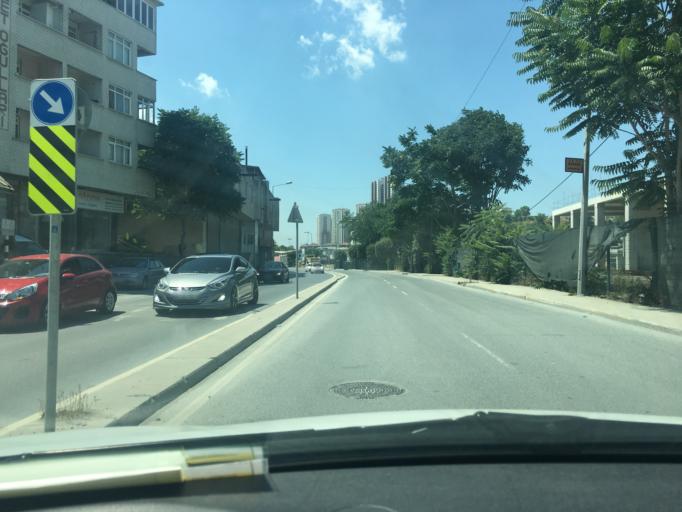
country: TR
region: Istanbul
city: Sisli
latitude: 41.0852
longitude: 28.9471
